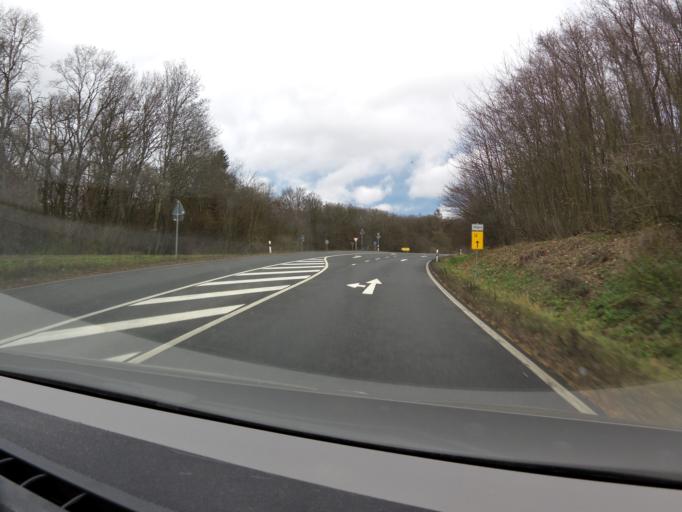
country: DE
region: Saxony-Anhalt
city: Blankenheim
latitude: 51.5313
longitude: 11.3787
